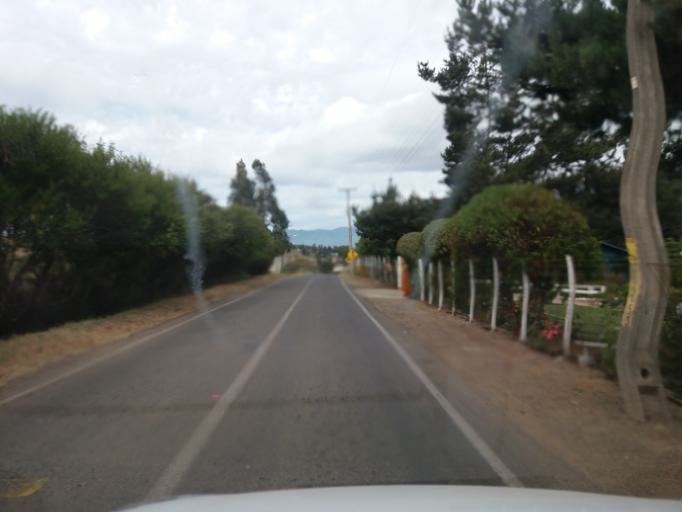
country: CL
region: Valparaiso
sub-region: Provincia de Marga Marga
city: Villa Alemana
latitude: -32.9171
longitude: -71.3821
